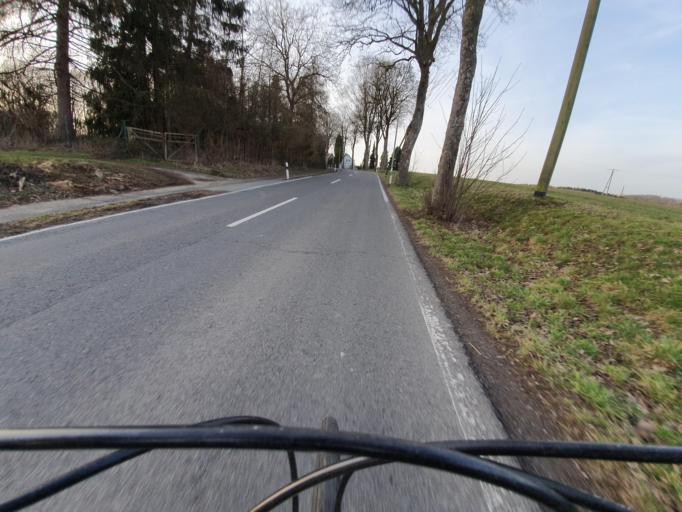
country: DE
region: North Rhine-Westphalia
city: Burscheid
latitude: 51.0907
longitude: 7.1597
